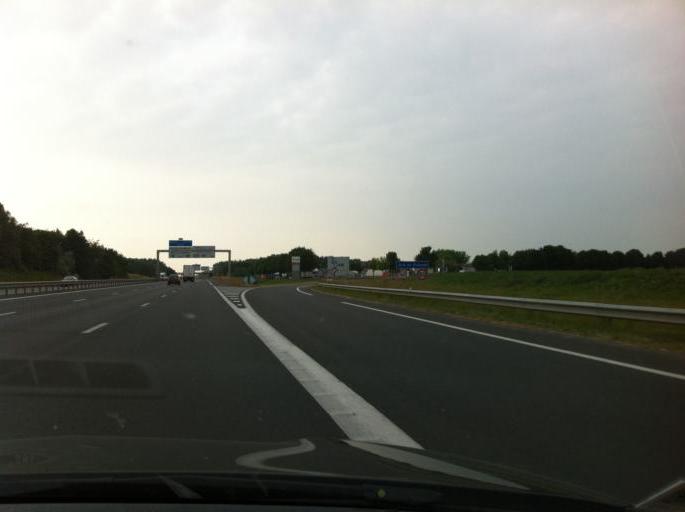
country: FR
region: Ile-de-France
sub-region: Departement de Seine-et-Marne
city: Moissy-Cramayel
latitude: 48.6074
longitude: 2.6332
